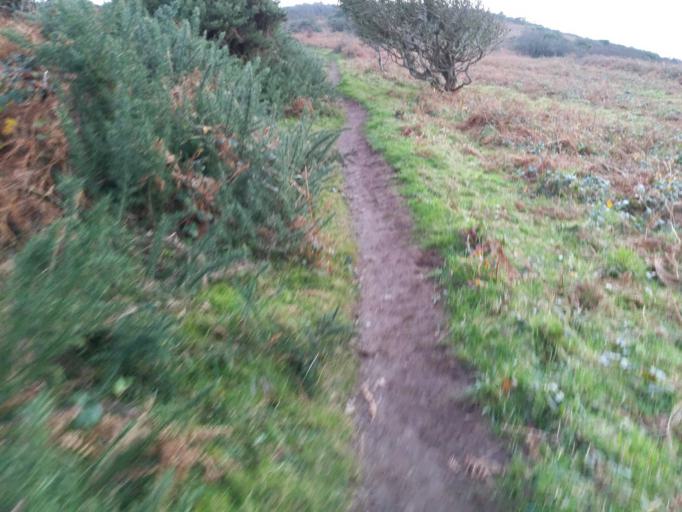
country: GB
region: England
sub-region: Cornwall
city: Fowey
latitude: 50.3262
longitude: -4.6008
